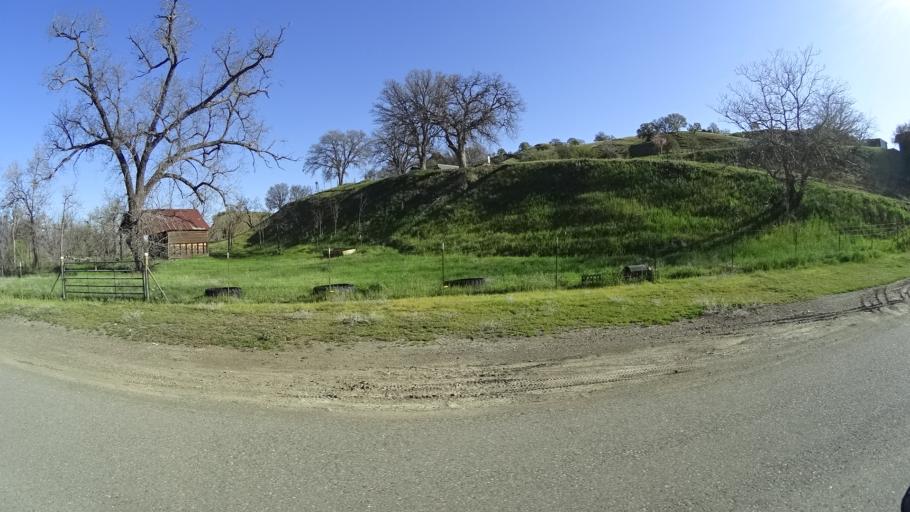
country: US
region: California
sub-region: Tehama County
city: Rancho Tehama Reserve
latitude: 39.7935
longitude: -122.5295
